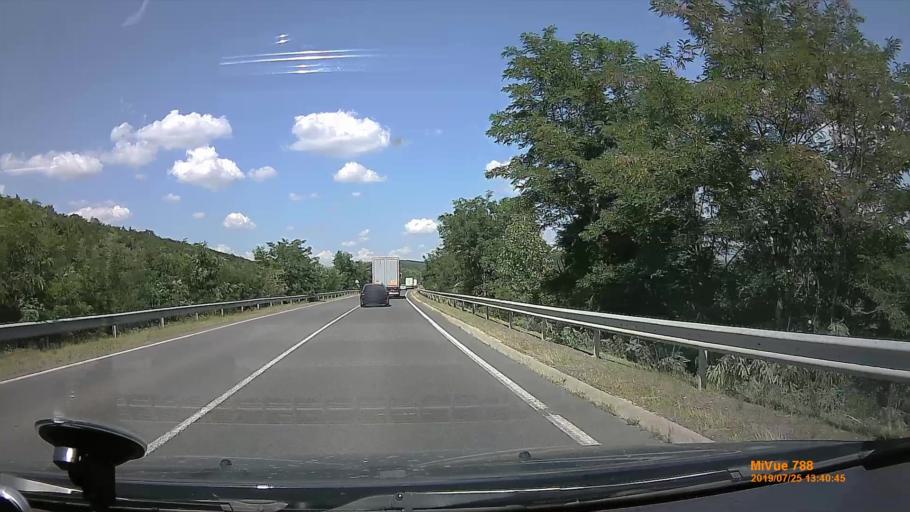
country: HU
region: Borsod-Abauj-Zemplen
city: Gonc
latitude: 48.4404
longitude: 21.1845
